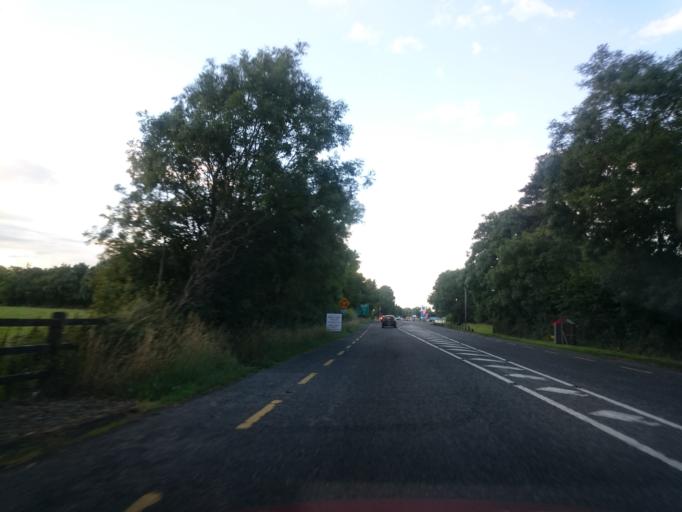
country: IE
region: Leinster
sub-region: Loch Garman
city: Loch Garman
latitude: 52.2986
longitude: -6.4595
